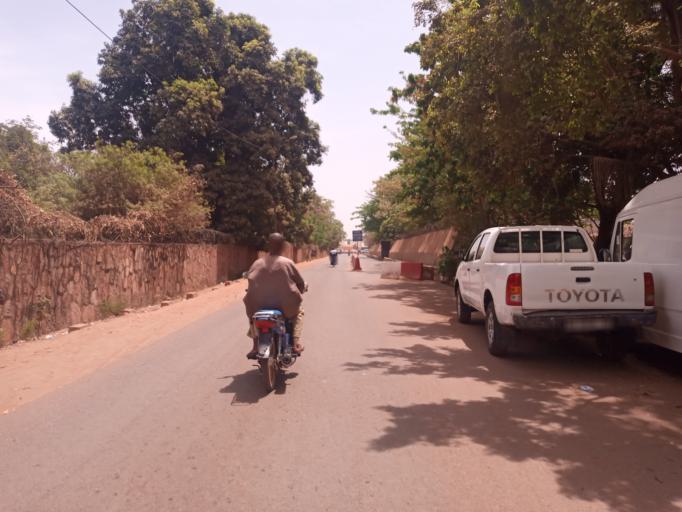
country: ML
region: Bamako
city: Bamako
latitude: 12.6373
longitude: -7.9942
